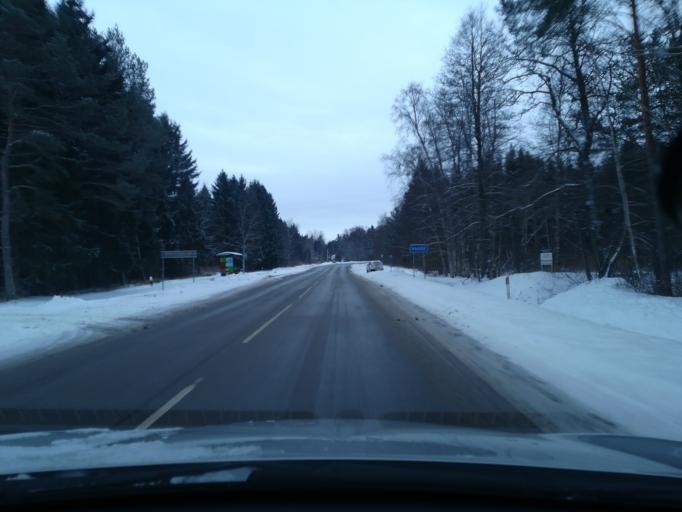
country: EE
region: Harju
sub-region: Keila linn
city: Keila
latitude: 59.4176
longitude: 24.3441
